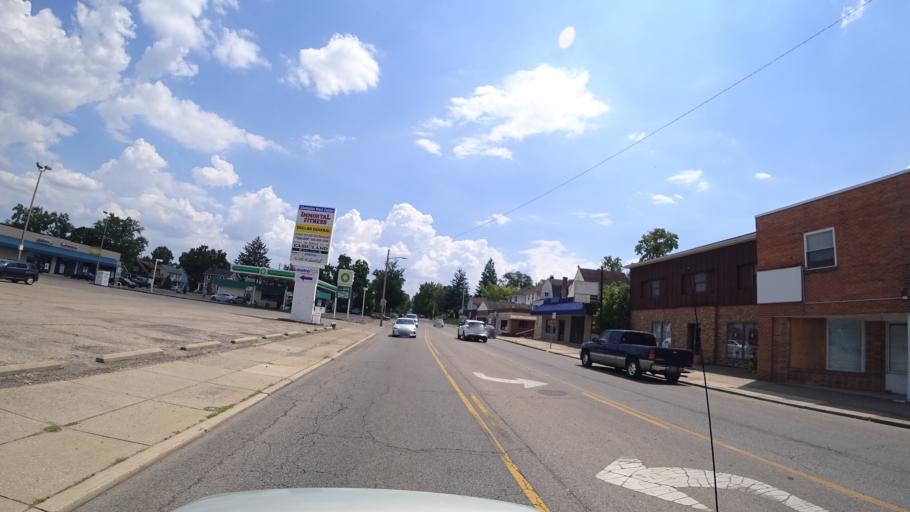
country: US
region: Ohio
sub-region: Butler County
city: Hamilton
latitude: 39.4124
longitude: -84.5803
